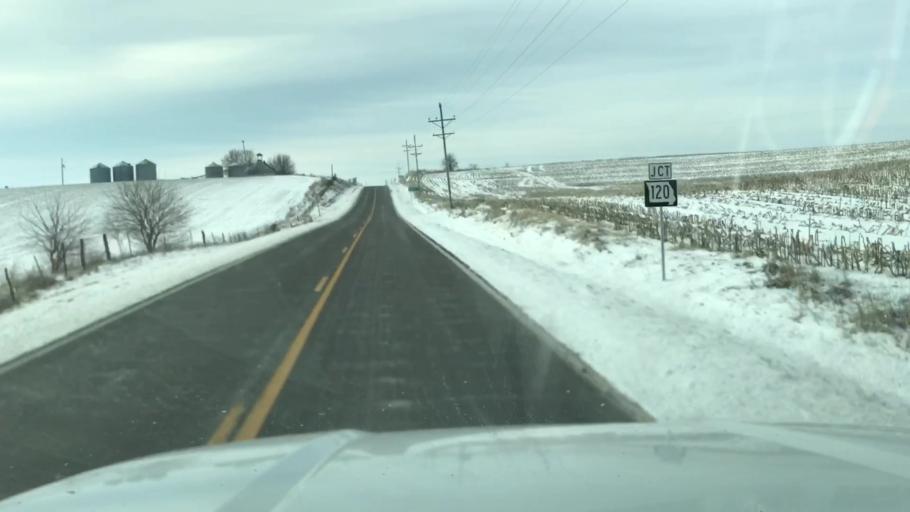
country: US
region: Missouri
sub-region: Holt County
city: Oregon
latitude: 40.0672
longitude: -95.1356
